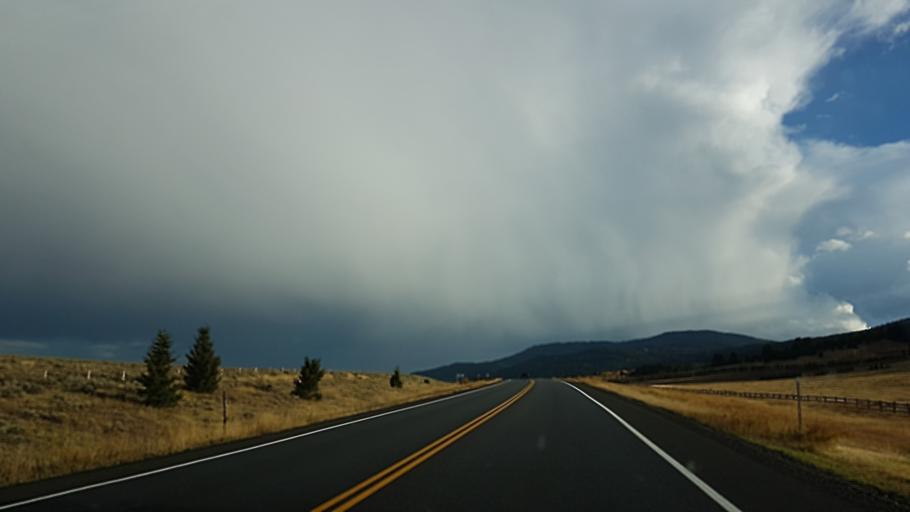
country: US
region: Montana
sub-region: Gallatin County
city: West Yellowstone
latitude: 44.7167
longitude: -111.4715
